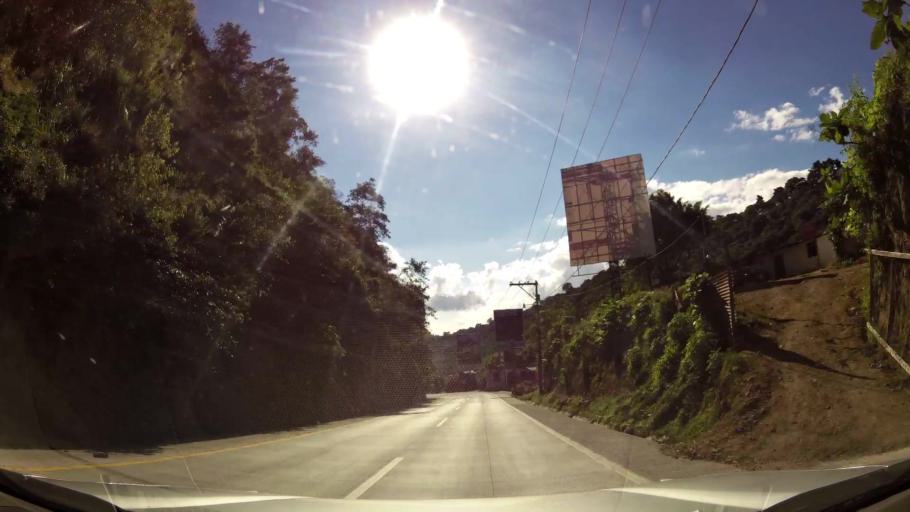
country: GT
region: Sacatepequez
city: Santa Lucia Milpas Altas
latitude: 14.5745
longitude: -90.6863
